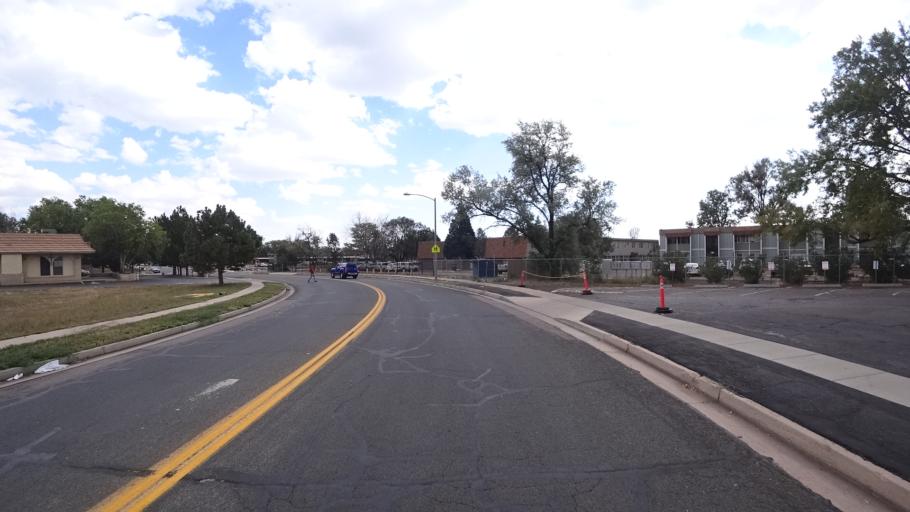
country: US
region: Colorado
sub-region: El Paso County
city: Cimarron Hills
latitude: 38.8510
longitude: -104.7536
